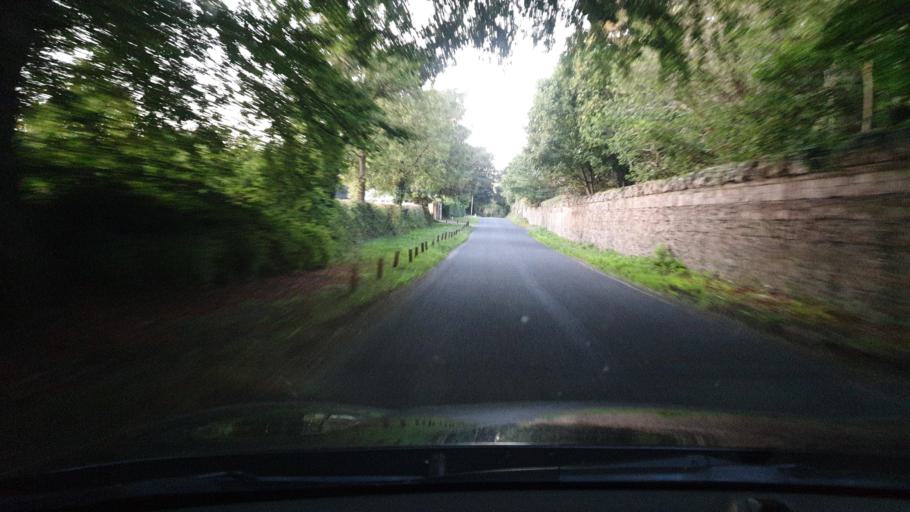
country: IE
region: Leinster
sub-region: Kildare
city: Prosperous
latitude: 53.3345
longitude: -6.7557
